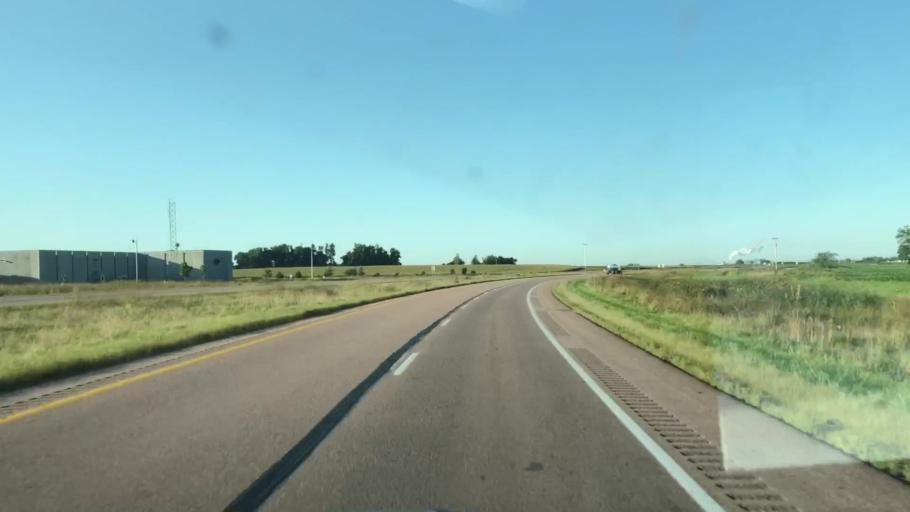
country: US
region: Iowa
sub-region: Osceola County
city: Sibley
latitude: 43.3079
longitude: -95.7795
